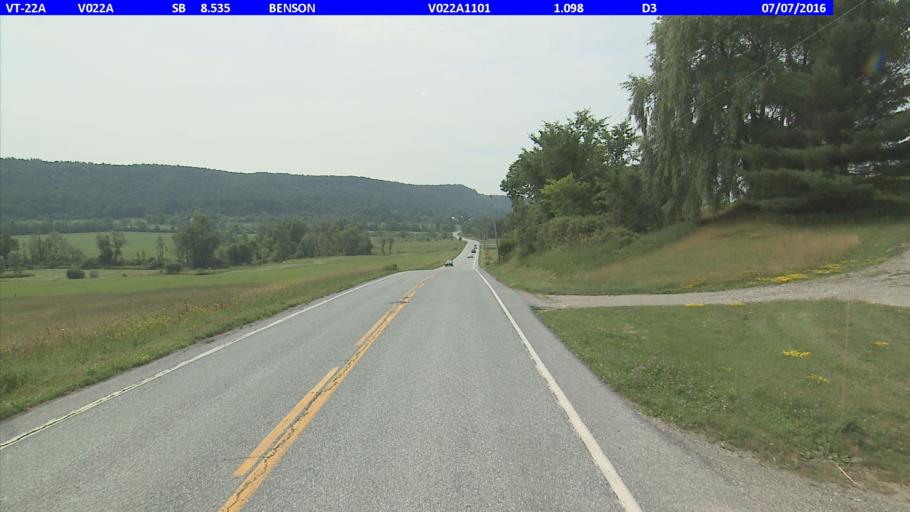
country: US
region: Vermont
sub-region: Rutland County
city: Fair Haven
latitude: 43.6850
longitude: -73.2898
